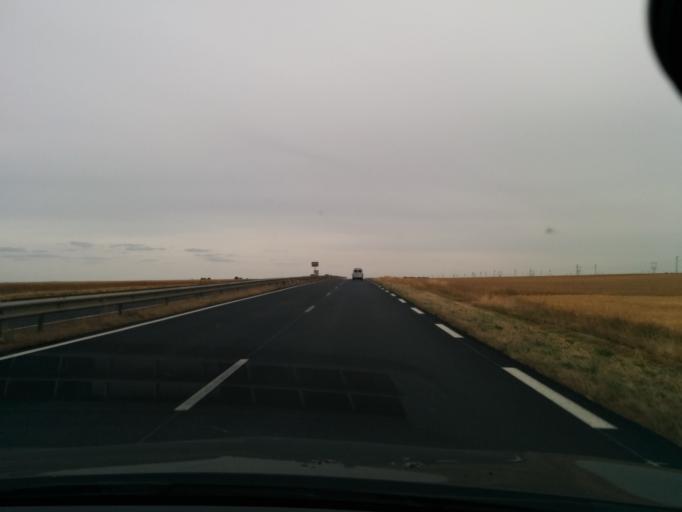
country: FR
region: Ile-de-France
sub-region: Departement de l'Essonne
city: Angerville
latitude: 48.2967
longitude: 1.9879
